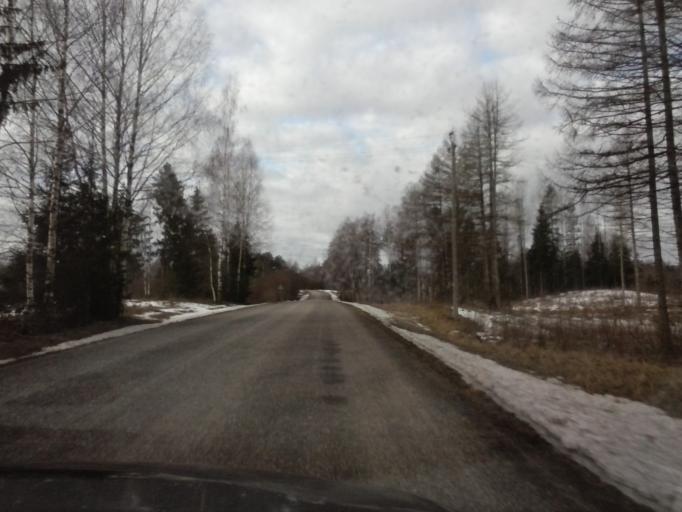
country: EE
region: Tartu
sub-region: Elva linn
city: Elva
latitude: 58.0027
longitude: 26.2783
